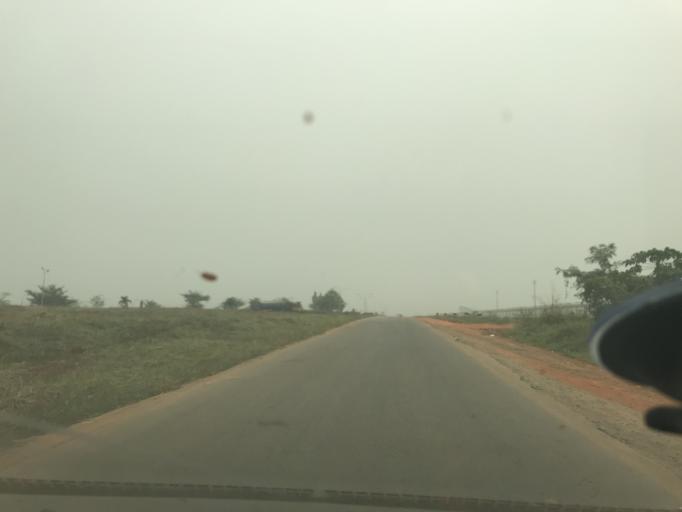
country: NG
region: Ogun
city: Owode
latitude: 6.8902
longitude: 3.5672
